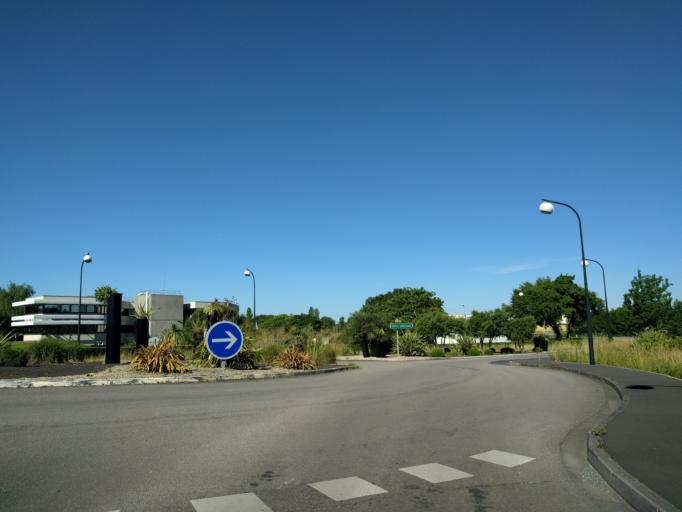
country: FR
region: Poitou-Charentes
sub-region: Departement des Deux-Sevres
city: Chauray
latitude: 46.3410
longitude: -0.4069
